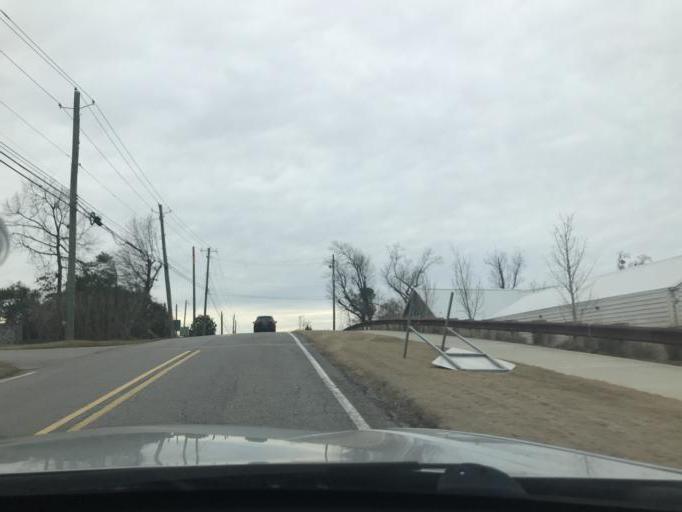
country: US
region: Alabama
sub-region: Jefferson County
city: Cahaba Heights
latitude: 33.4559
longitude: -86.7309
